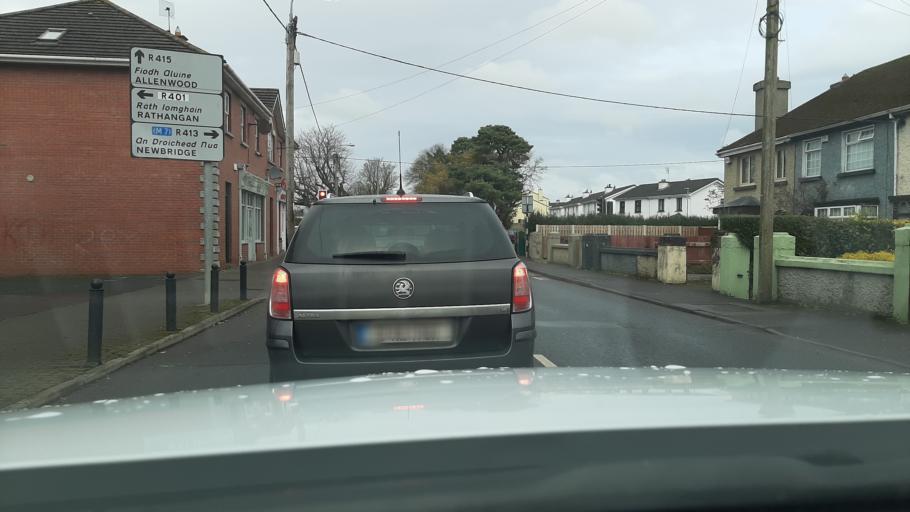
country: IE
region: Leinster
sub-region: Kildare
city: Kildare
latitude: 53.1594
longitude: -6.9093
